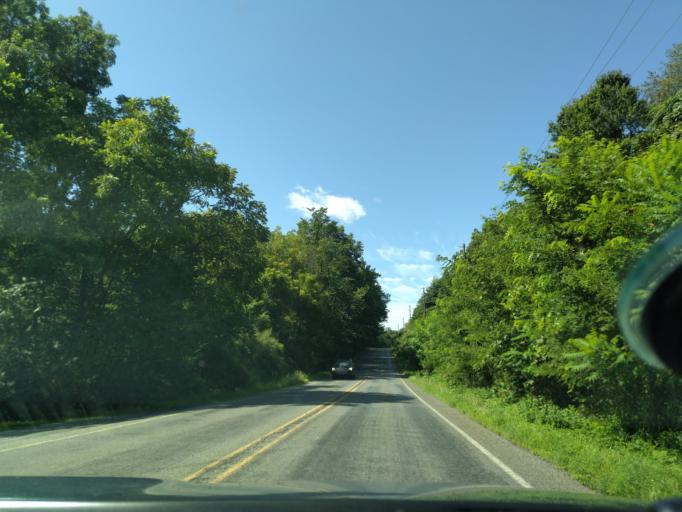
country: US
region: Pennsylvania
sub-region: Pike County
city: Saw Creek
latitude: 41.1035
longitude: -74.9886
